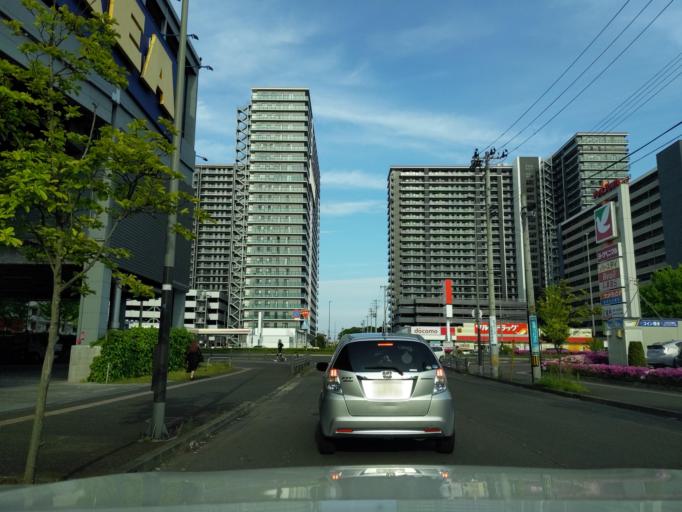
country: JP
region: Miyagi
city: Sendai
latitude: 38.2248
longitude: 140.8862
